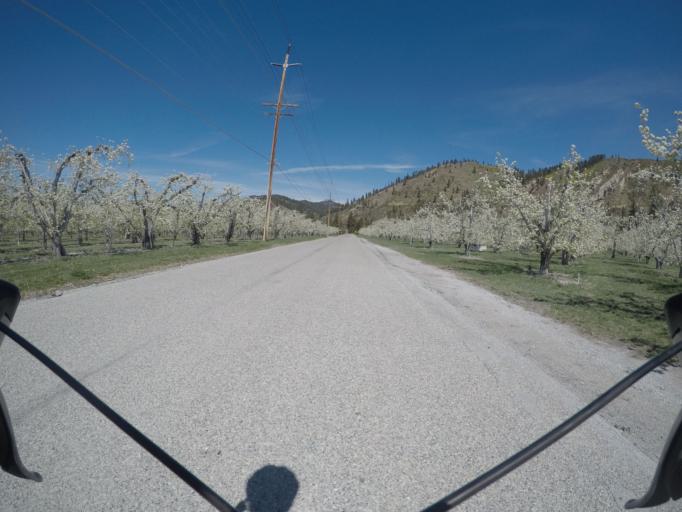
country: US
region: Washington
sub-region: Chelan County
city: Leavenworth
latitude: 47.5608
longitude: -120.5824
